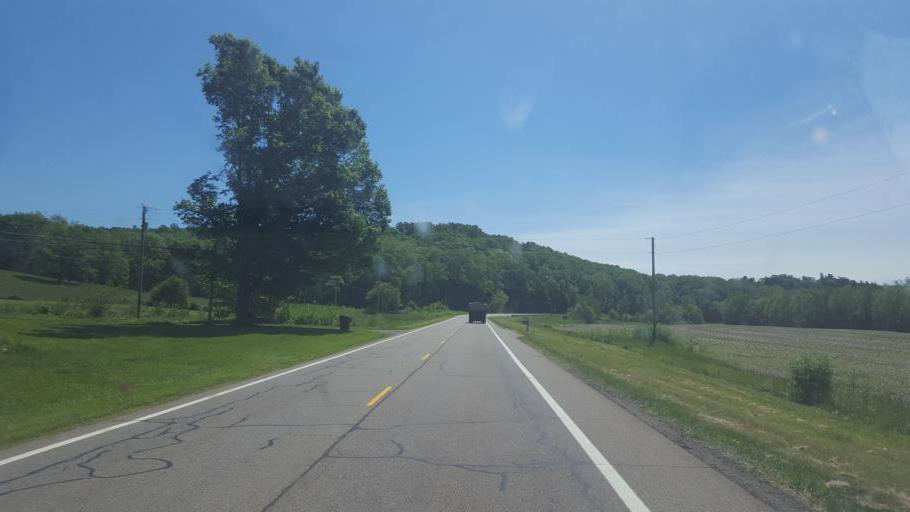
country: US
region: Ohio
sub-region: Knox County
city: Gambier
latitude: 40.3794
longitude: -82.4107
